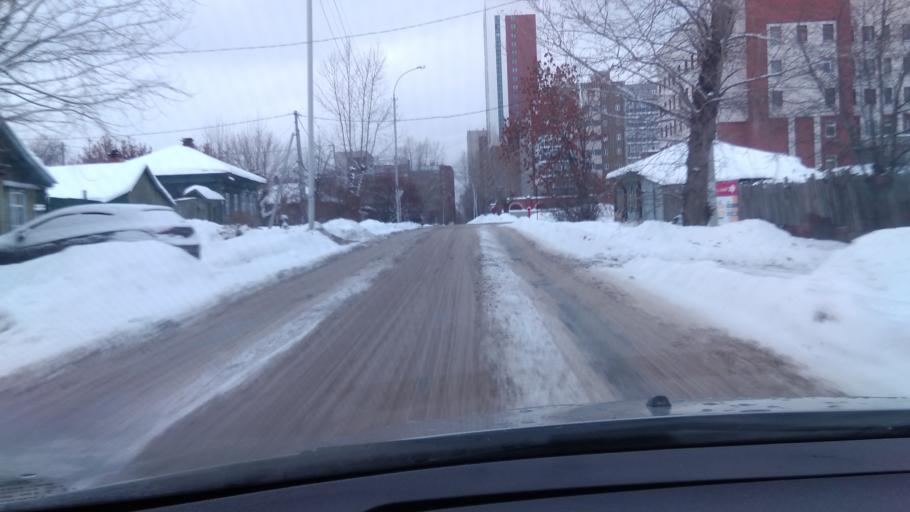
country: RU
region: Sverdlovsk
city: Yekaterinburg
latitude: 56.8035
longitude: 60.5970
